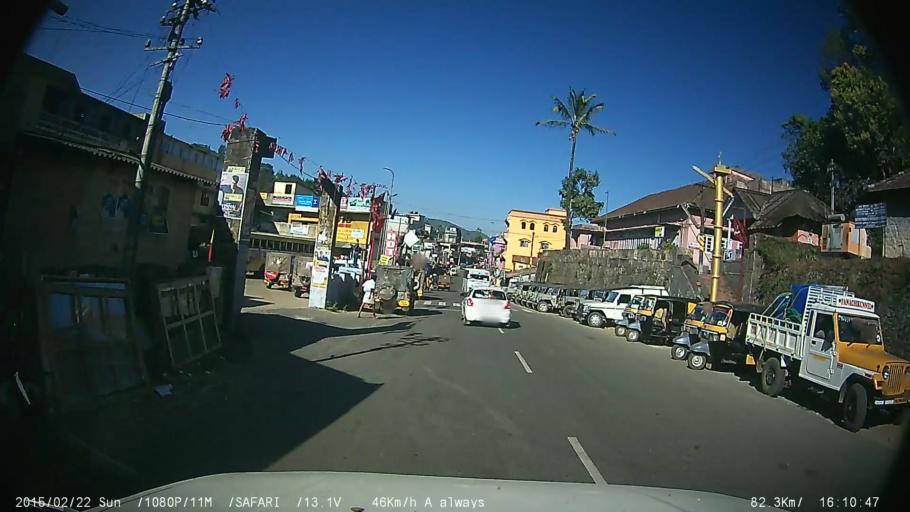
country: IN
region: Tamil Nadu
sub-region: Theni
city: Gudalur
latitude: 9.5710
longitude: 77.0886
